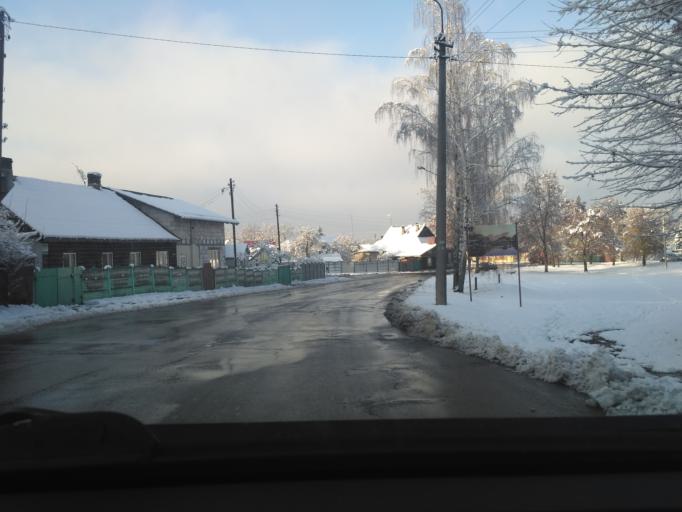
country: BY
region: Minsk
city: Horad Barysaw
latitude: 54.2343
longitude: 28.4976
